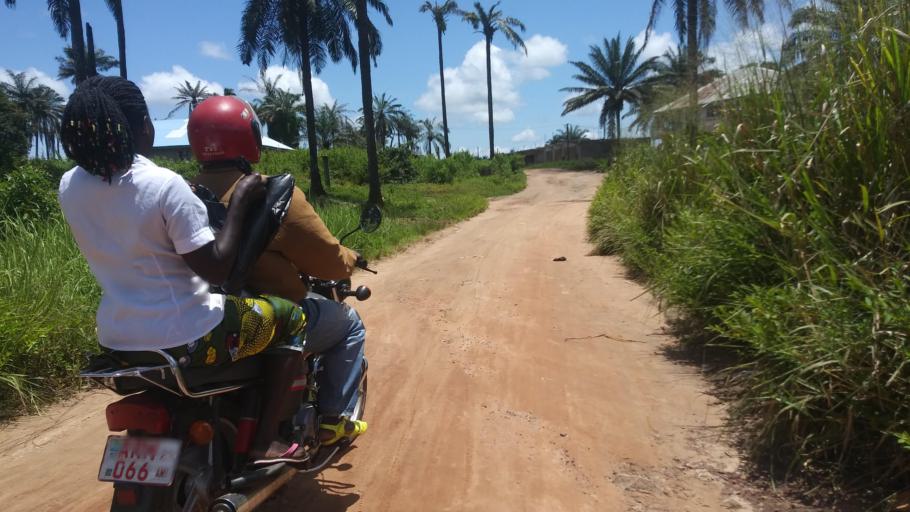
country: SL
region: Northern Province
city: Makeni
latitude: 8.8791
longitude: -12.0200
